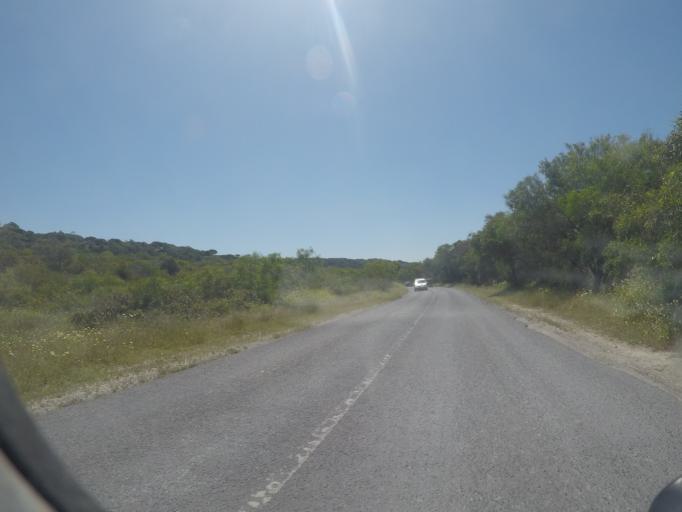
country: PT
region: Setubal
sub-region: Almada
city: Charneca
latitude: 38.6107
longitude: -9.2076
